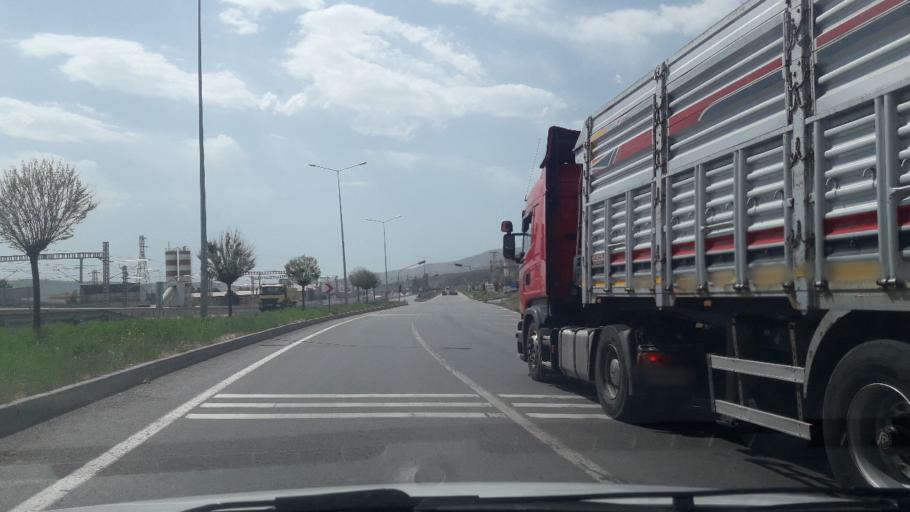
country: TR
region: Sivas
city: Sivas
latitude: 39.7184
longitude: 36.9446
